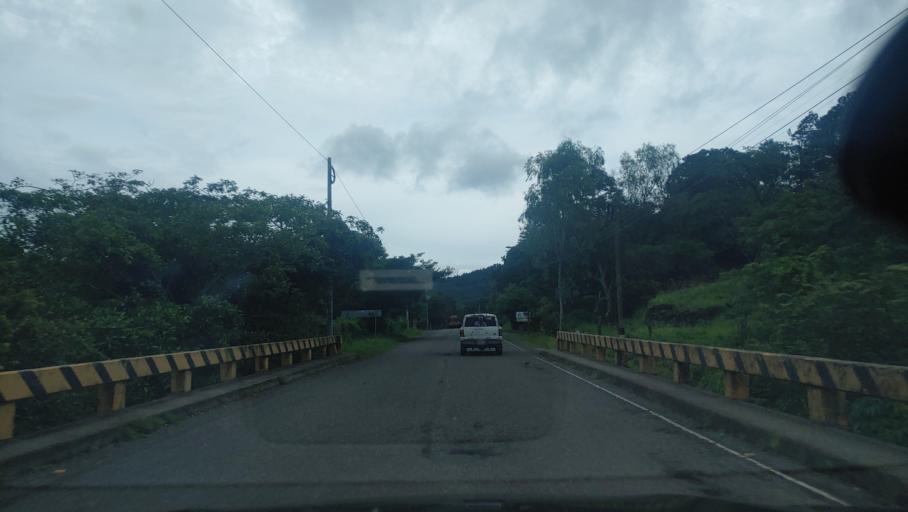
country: HN
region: Choluteca
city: San Marcos de Colon
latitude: 13.3776
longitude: -86.8798
